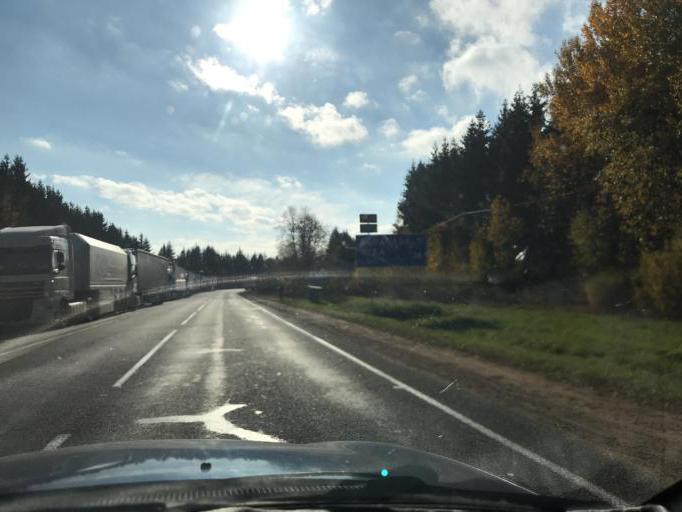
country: LT
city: Salcininkai
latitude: 54.2318
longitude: 25.3579
